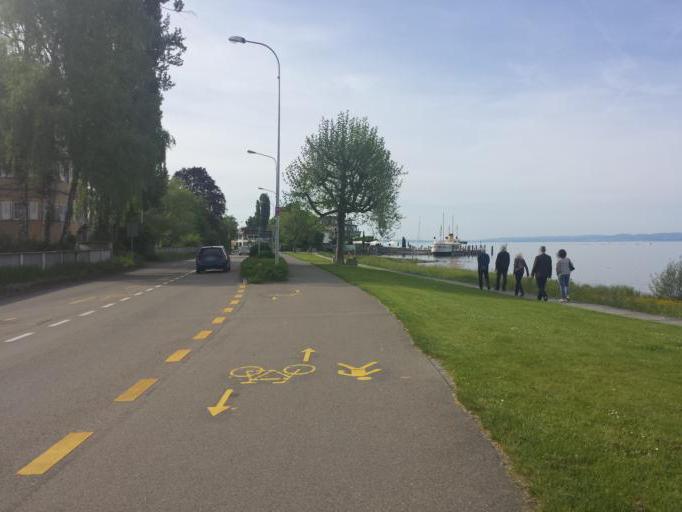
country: CH
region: Saint Gallen
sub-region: Wahlkreis Rorschach
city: Horn
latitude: 47.4927
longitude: 9.4705
